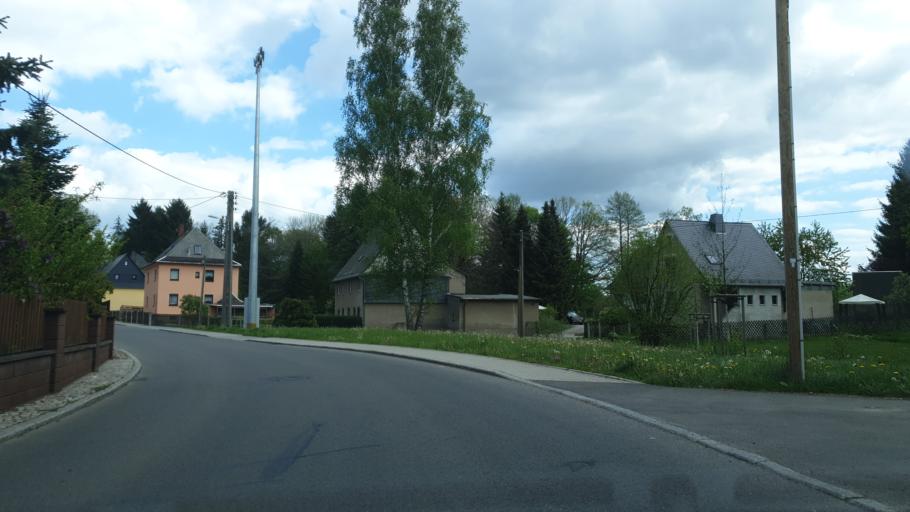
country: DE
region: Saxony
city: Kirchberg
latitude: 50.7900
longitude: 12.7626
